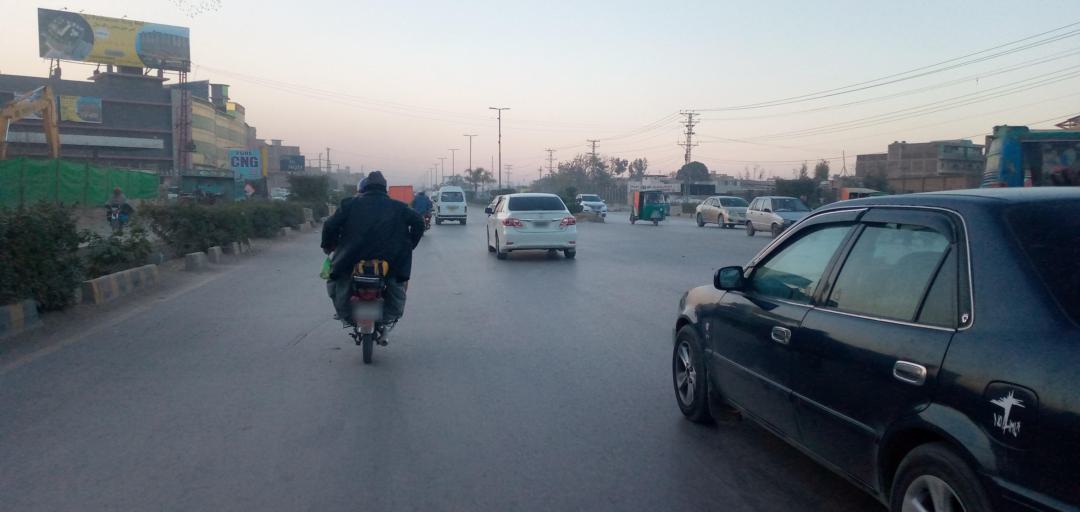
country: PK
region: Khyber Pakhtunkhwa
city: Peshawar
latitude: 34.0290
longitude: 71.6141
